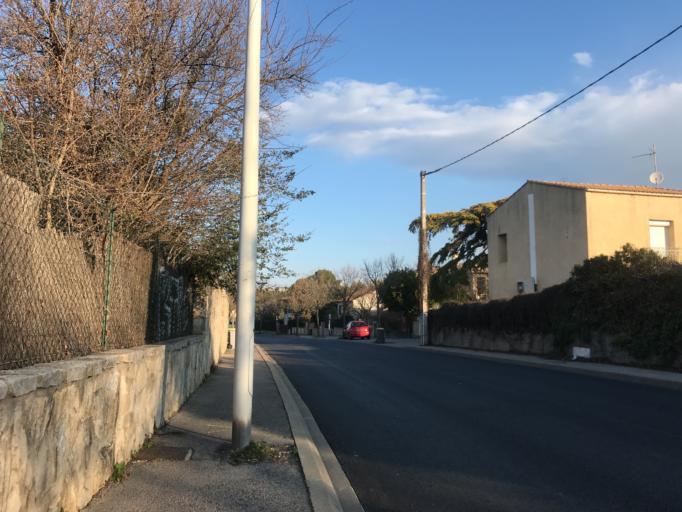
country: FR
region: Languedoc-Roussillon
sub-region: Departement de l'Herault
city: Castelnau-le-Lez
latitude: 43.6333
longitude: 3.8778
